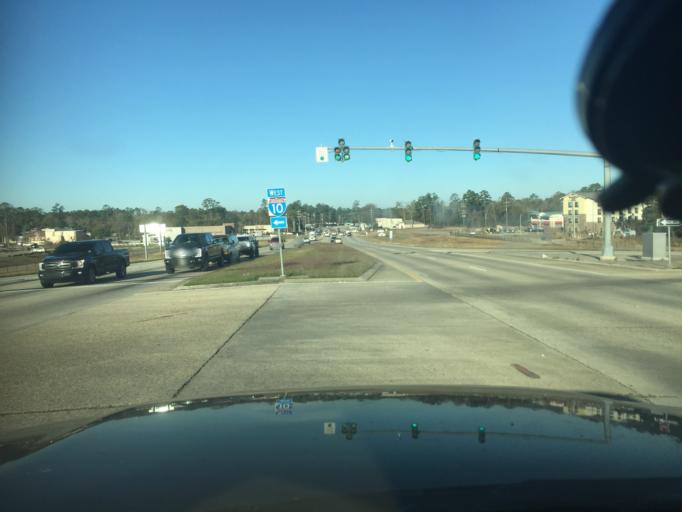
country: US
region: Louisiana
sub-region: Saint Tammany Parish
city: Slidell
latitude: 30.2706
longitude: -89.7560
